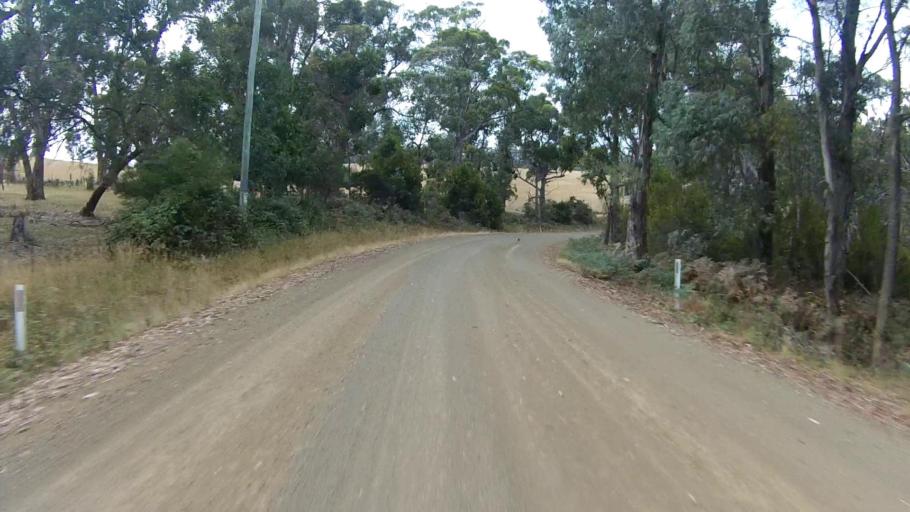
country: AU
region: Tasmania
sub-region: Huon Valley
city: Cygnet
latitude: -43.2373
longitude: 147.0996
